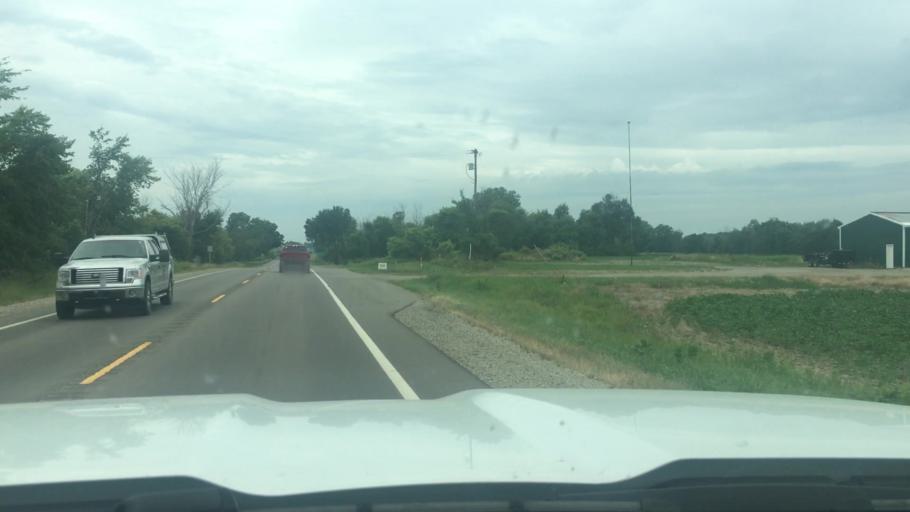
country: US
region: Michigan
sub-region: Clinton County
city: Fowler
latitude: 43.0016
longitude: -84.6543
